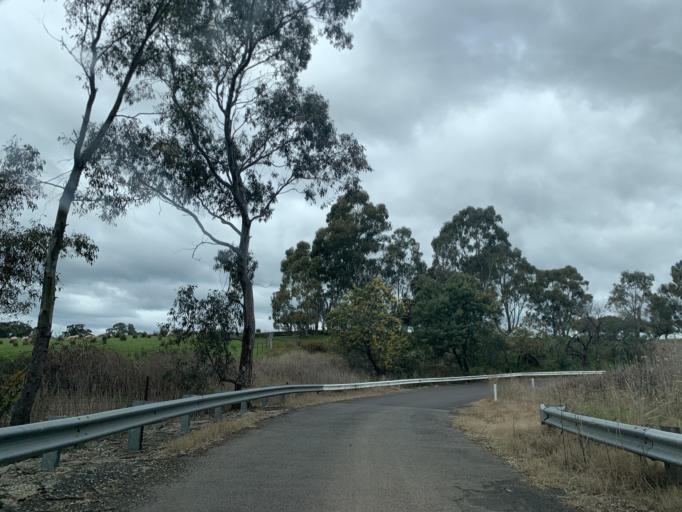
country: AU
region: Victoria
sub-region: Whittlesea
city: Whittlesea
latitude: -37.1218
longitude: 144.9366
